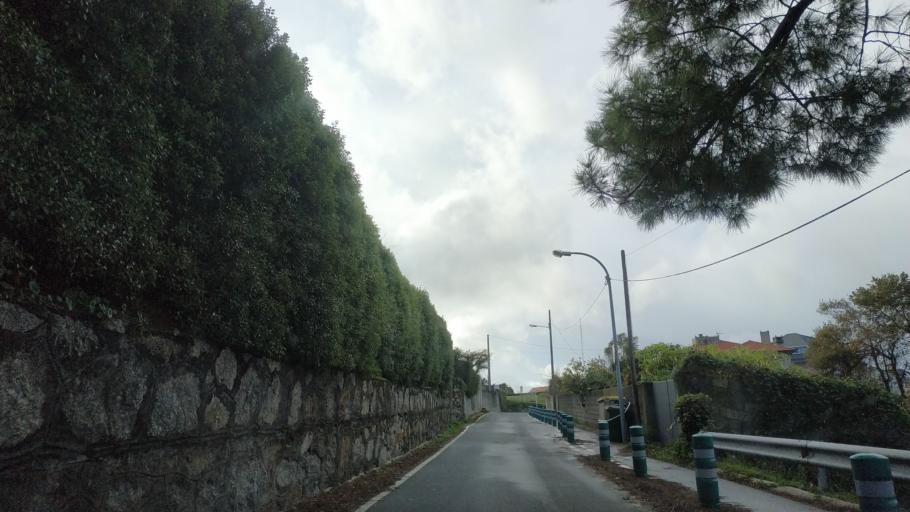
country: ES
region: Galicia
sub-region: Provincia da Coruna
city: Culleredo
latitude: 43.3284
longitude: -8.4010
